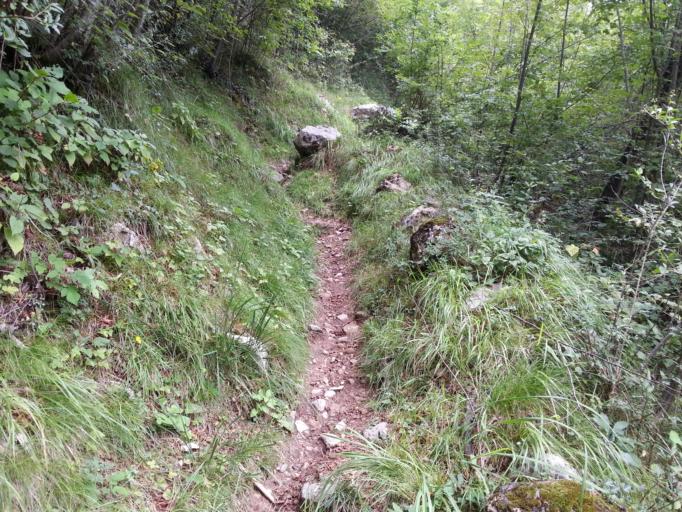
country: IT
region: Lombardy
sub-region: Provincia di Lecco
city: Cortenova
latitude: 45.9933
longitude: 9.3850
